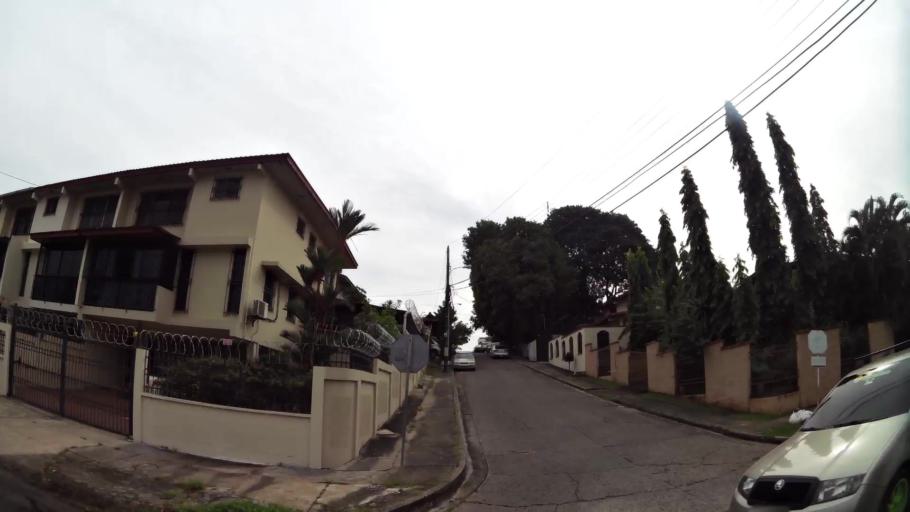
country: PA
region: Panama
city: Panama
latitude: 9.0131
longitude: -79.5192
